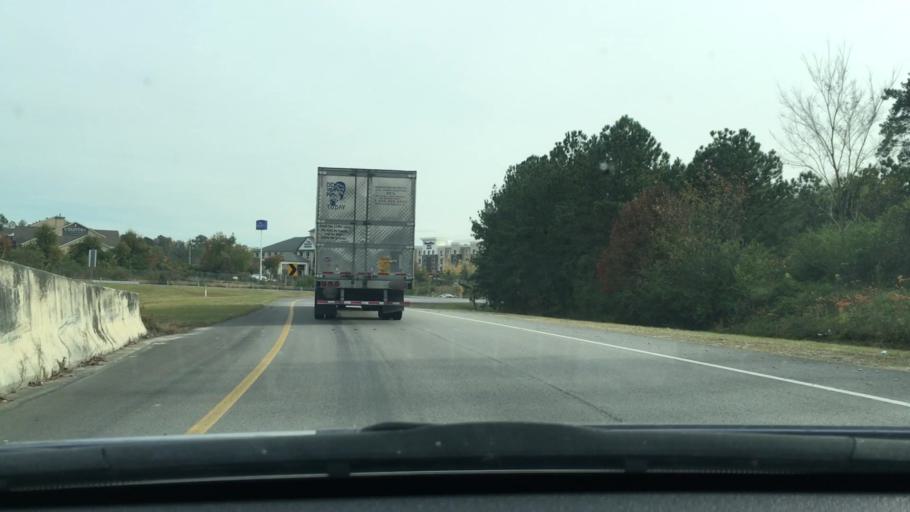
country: US
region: South Carolina
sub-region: Richland County
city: Forest Acres
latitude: 33.9694
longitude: -80.9551
